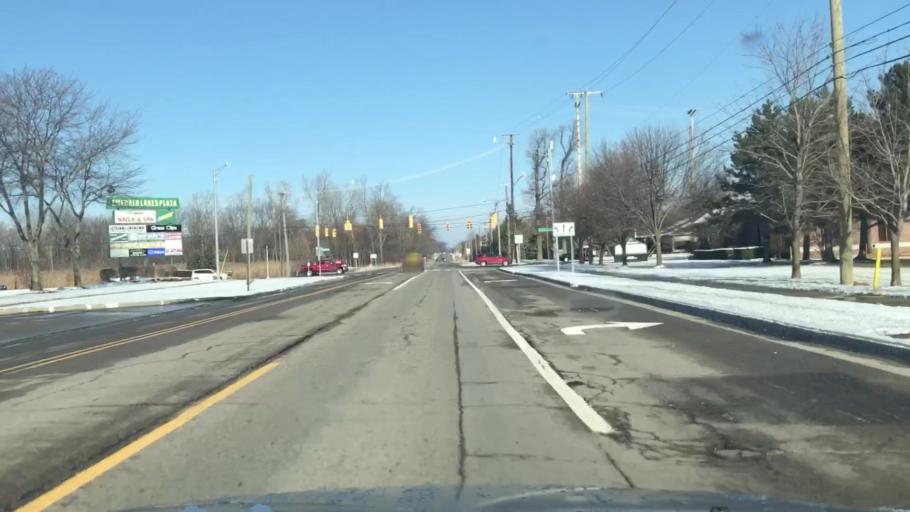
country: US
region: Michigan
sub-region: Oakland County
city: Troy
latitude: 42.6065
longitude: -83.1101
